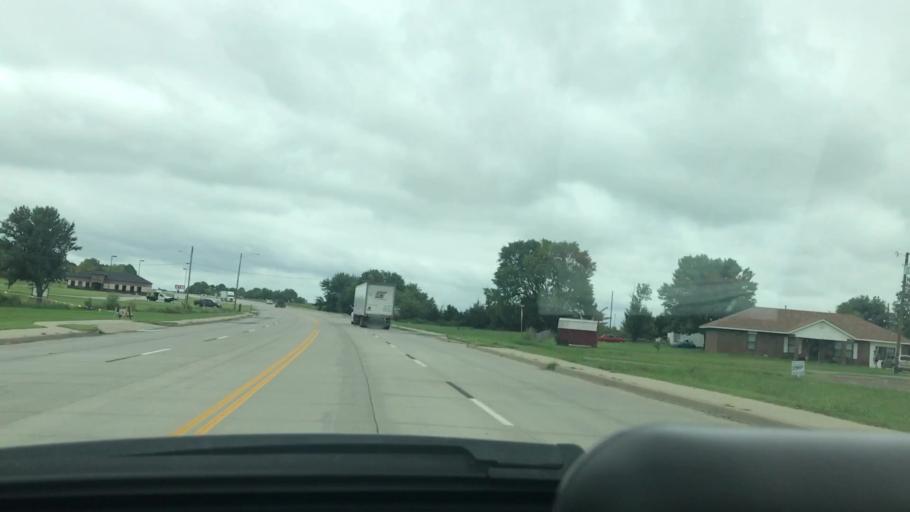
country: US
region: Oklahoma
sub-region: Pittsburg County
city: McAlester
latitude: 34.7250
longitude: -95.8983
